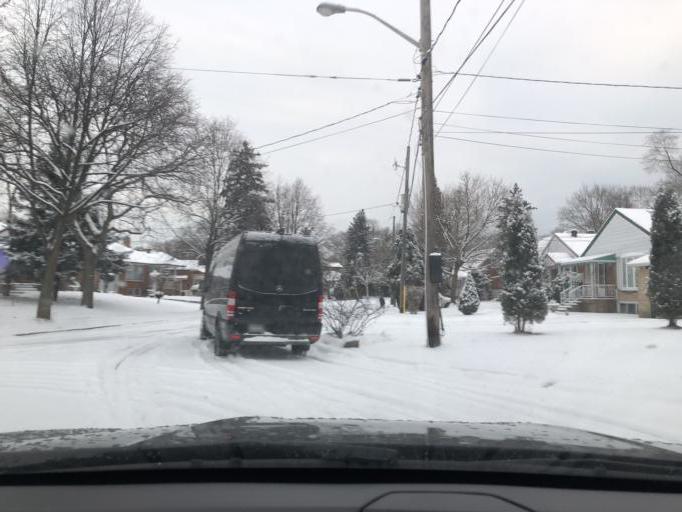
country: CA
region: Ontario
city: Toronto
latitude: 43.7031
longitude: -79.4894
